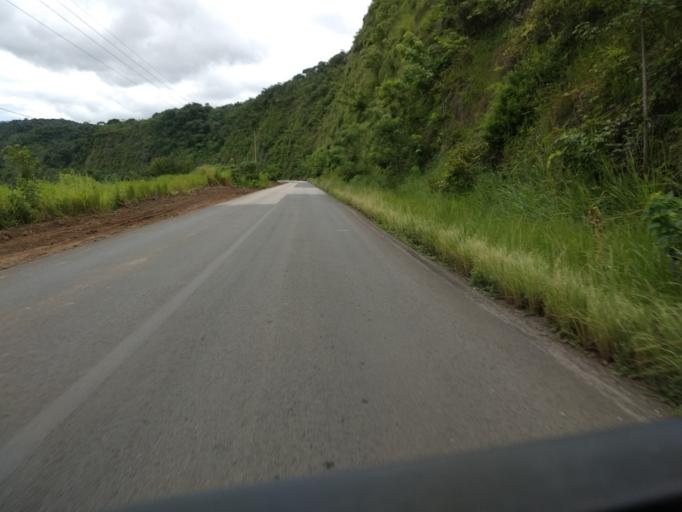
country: CR
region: Puntarenas
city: Buenos Aires
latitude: 9.0893
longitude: -83.2726
